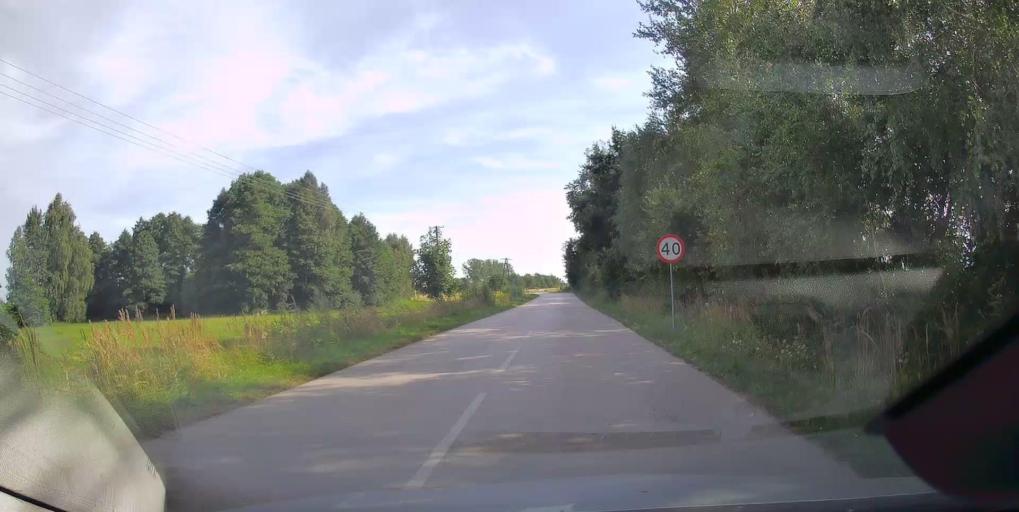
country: PL
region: Lodz Voivodeship
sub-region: Powiat opoczynski
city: Mniszkow
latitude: 51.3560
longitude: 20.0371
